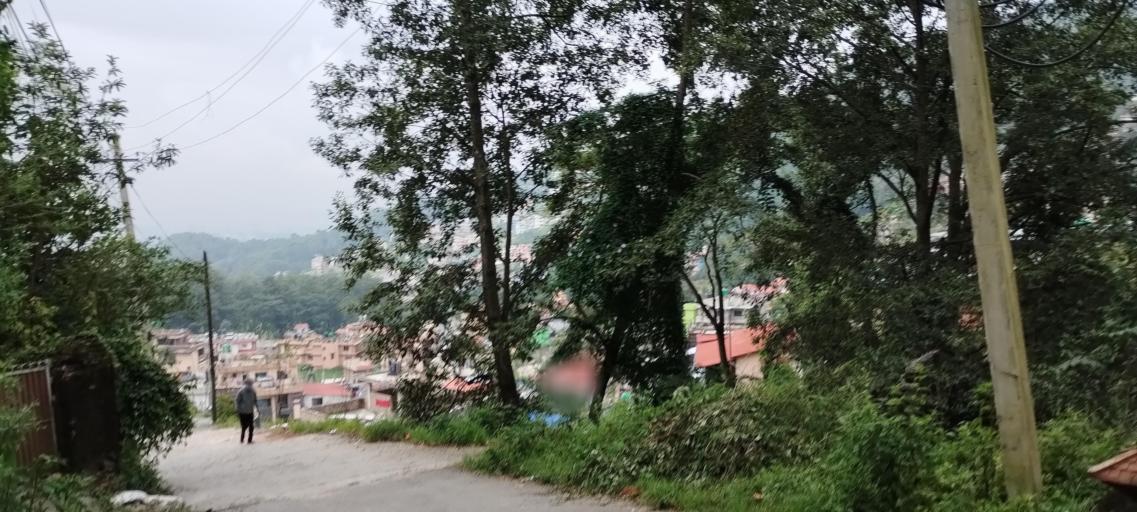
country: NP
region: Central Region
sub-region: Bagmati Zone
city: Kathmandu
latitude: 27.7862
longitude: 85.3601
